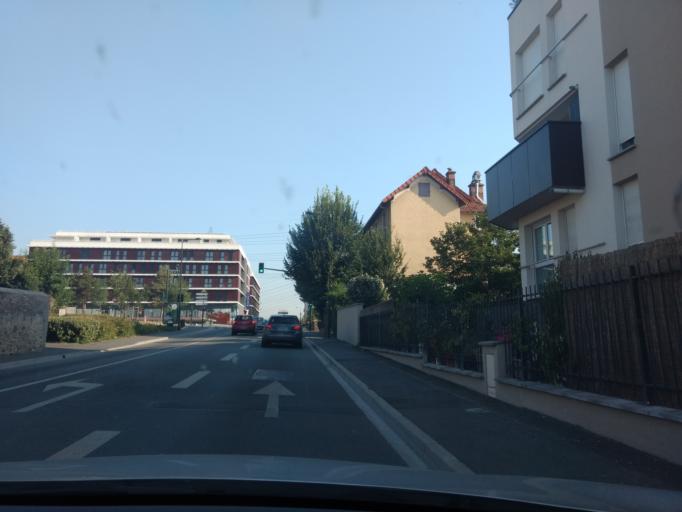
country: FR
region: Ile-de-France
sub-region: Departement de l'Essonne
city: Palaiseau
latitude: 48.7204
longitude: 2.2488
